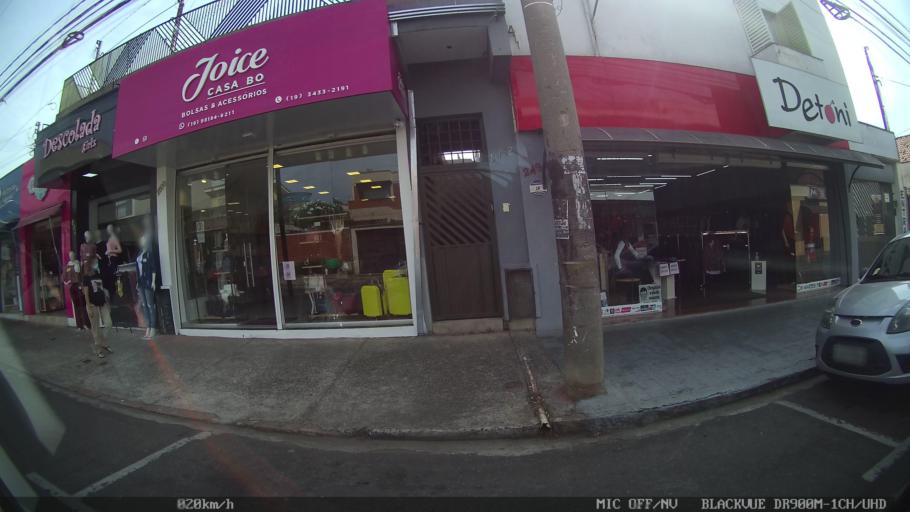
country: BR
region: Sao Paulo
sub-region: Piracicaba
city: Piracicaba
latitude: -22.7364
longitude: -47.6580
